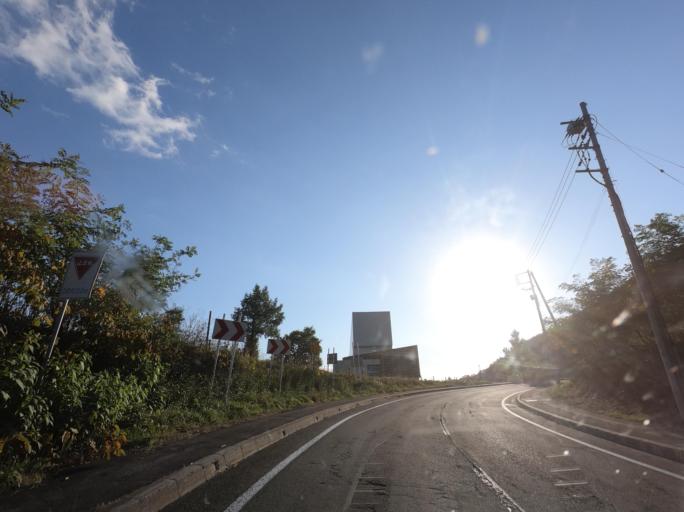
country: JP
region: Hokkaido
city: Iwamizawa
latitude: 43.0525
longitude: 141.9695
